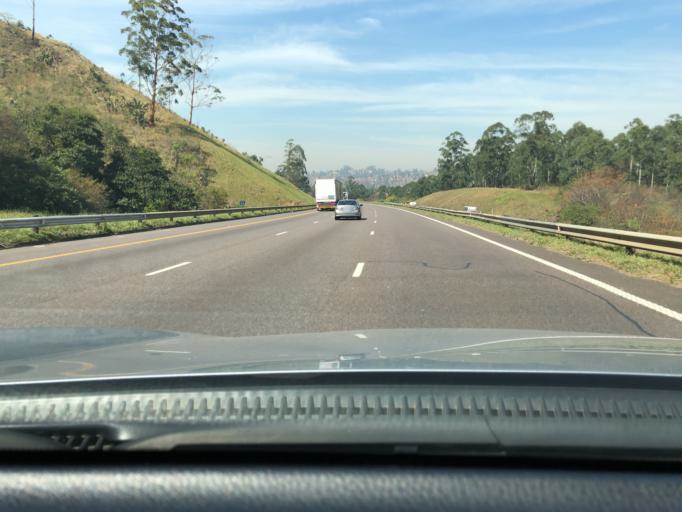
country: ZA
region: KwaZulu-Natal
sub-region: eThekwini Metropolitan Municipality
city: Mpumalanga
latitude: -29.8174
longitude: 30.7746
